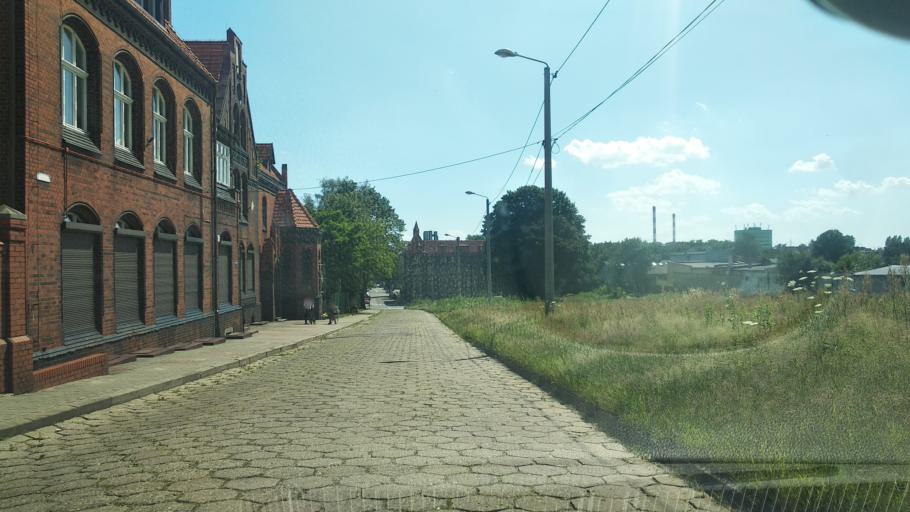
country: PL
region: Silesian Voivodeship
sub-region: Sosnowiec
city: Sosnowiec
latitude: 50.2670
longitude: 19.0960
